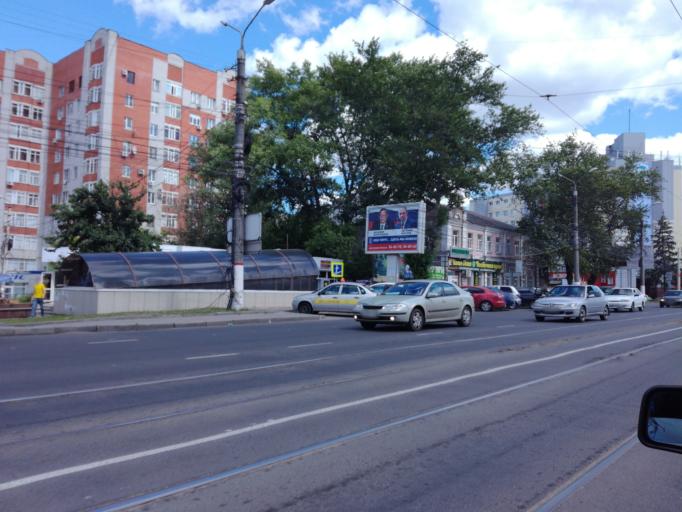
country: RU
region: Kursk
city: Kursk
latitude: 51.7508
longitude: 36.1922
